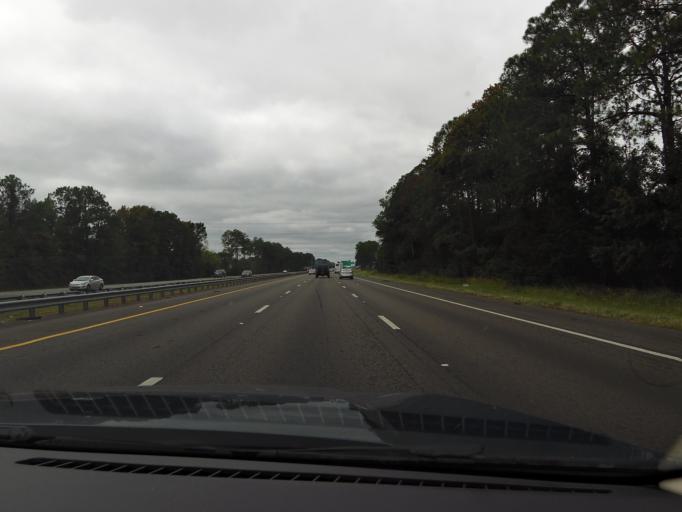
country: US
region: Florida
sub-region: Duval County
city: Baldwin
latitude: 30.3112
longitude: -81.8290
